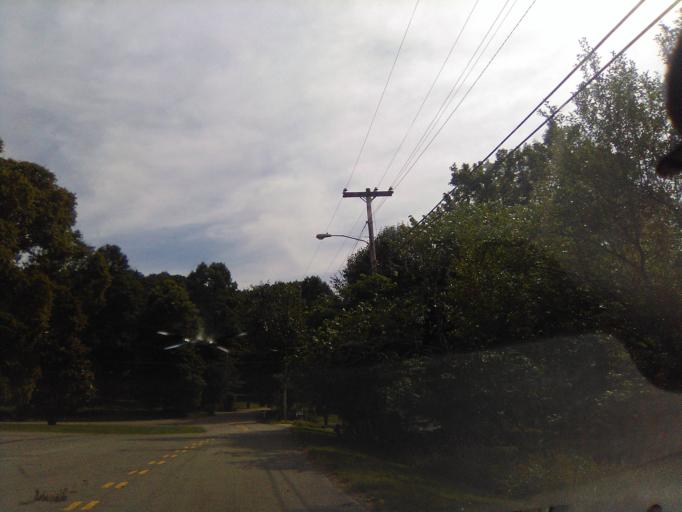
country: US
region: Tennessee
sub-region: Davidson County
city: Belle Meade
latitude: 36.1008
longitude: -86.9080
